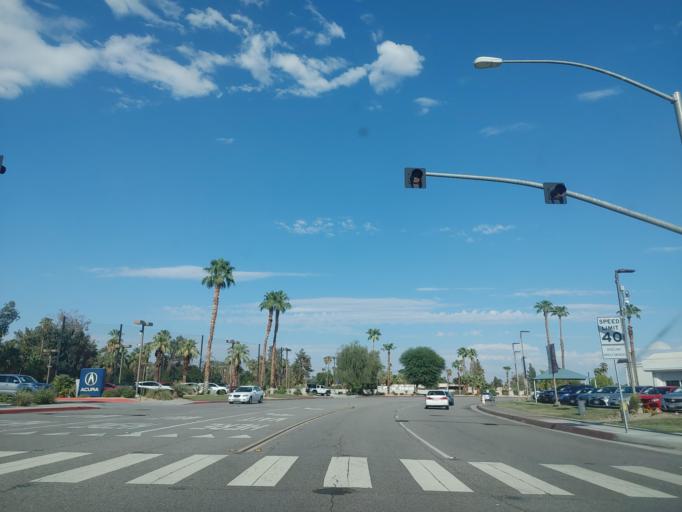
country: US
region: California
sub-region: Riverside County
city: Cathedral City
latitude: 33.7859
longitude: -116.4742
